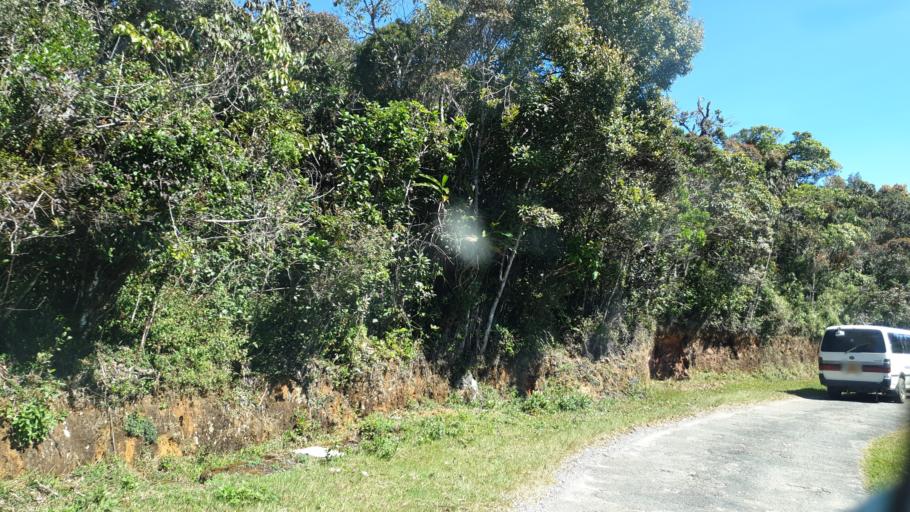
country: LK
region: Uva
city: Haputale
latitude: 6.7981
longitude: 80.8305
